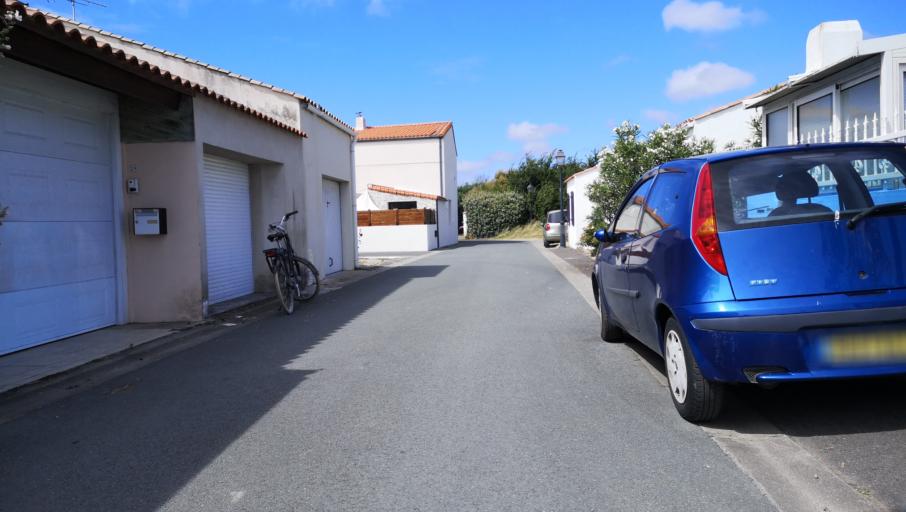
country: FR
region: Pays de la Loire
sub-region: Departement de la Vendee
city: Les Sables-d'Olonne
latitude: 46.5136
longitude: -1.7965
